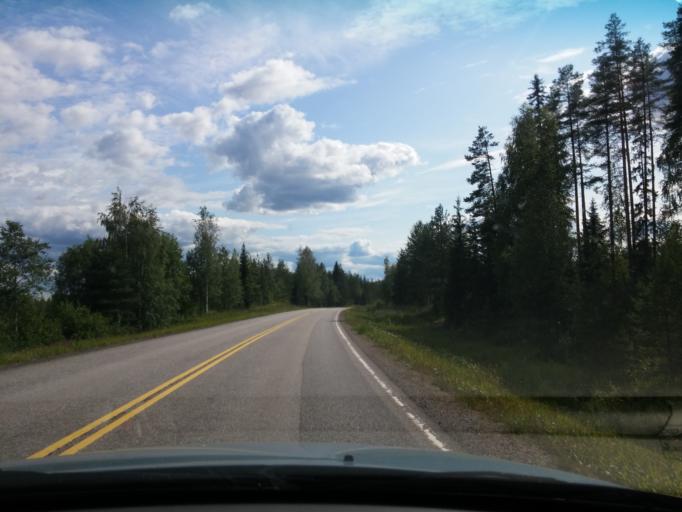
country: FI
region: Central Finland
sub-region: Keuruu
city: Keuruu
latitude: 62.3233
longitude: 24.7337
